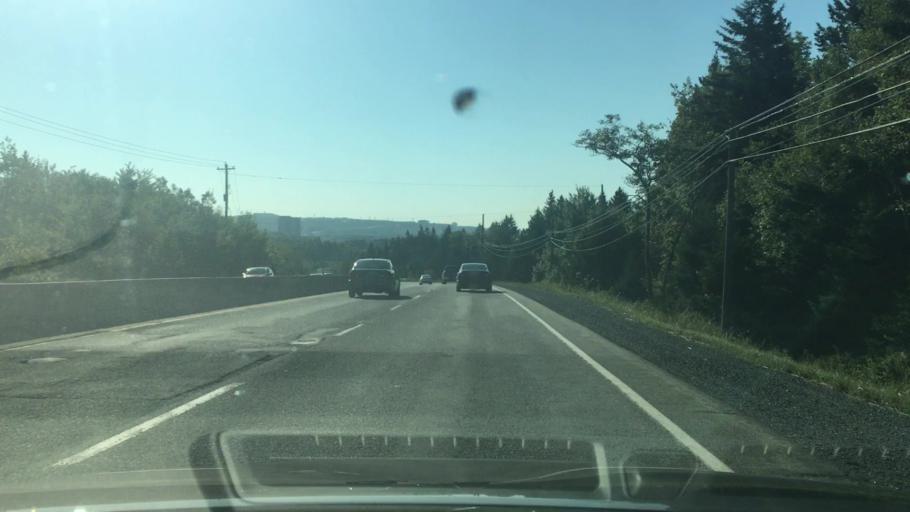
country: CA
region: Nova Scotia
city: Dartmouth
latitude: 44.7100
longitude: -63.6260
